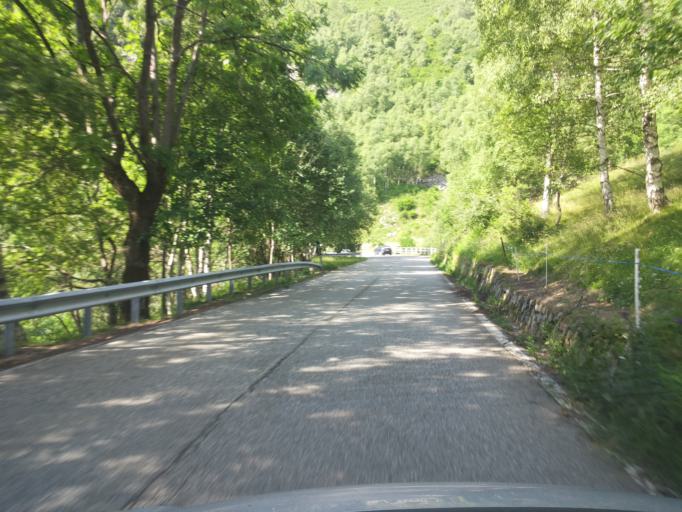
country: IT
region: Piedmont
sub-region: Provincia di Biella
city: Quittengo
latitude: 45.6615
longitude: 8.0307
